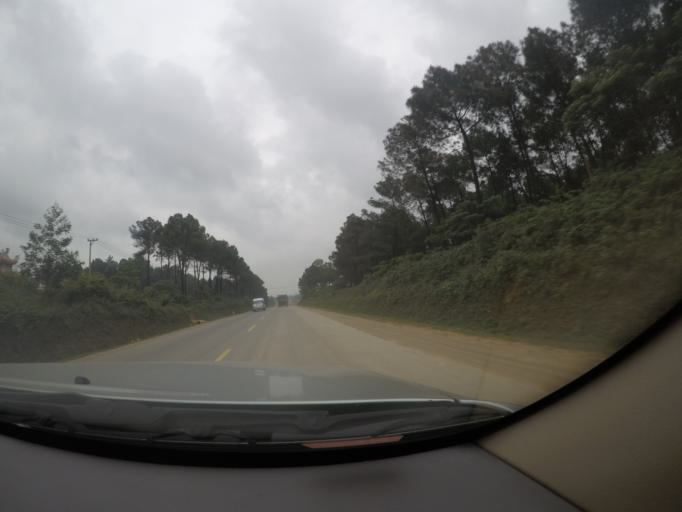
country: VN
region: Quang Tri
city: Dong Ha
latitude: 16.7899
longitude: 107.0740
